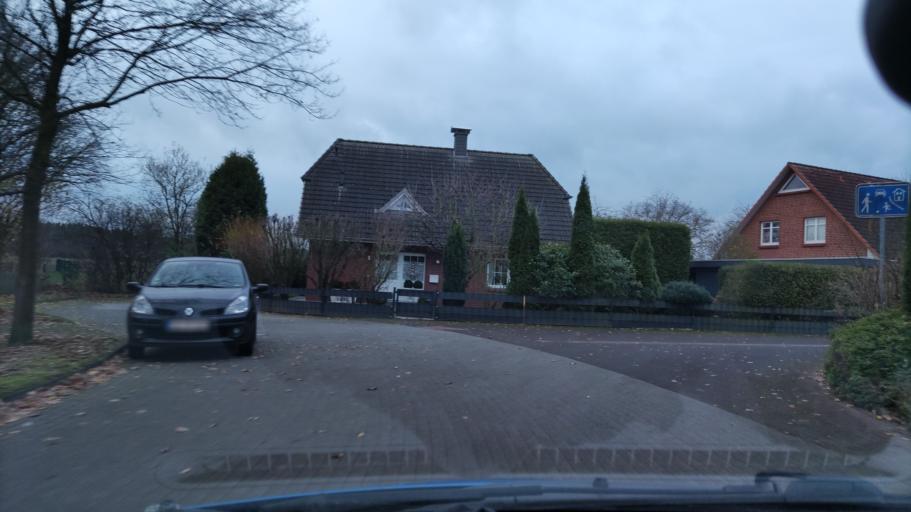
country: DE
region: Lower Saxony
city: Vogelsen
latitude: 53.2720
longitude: 10.3506
